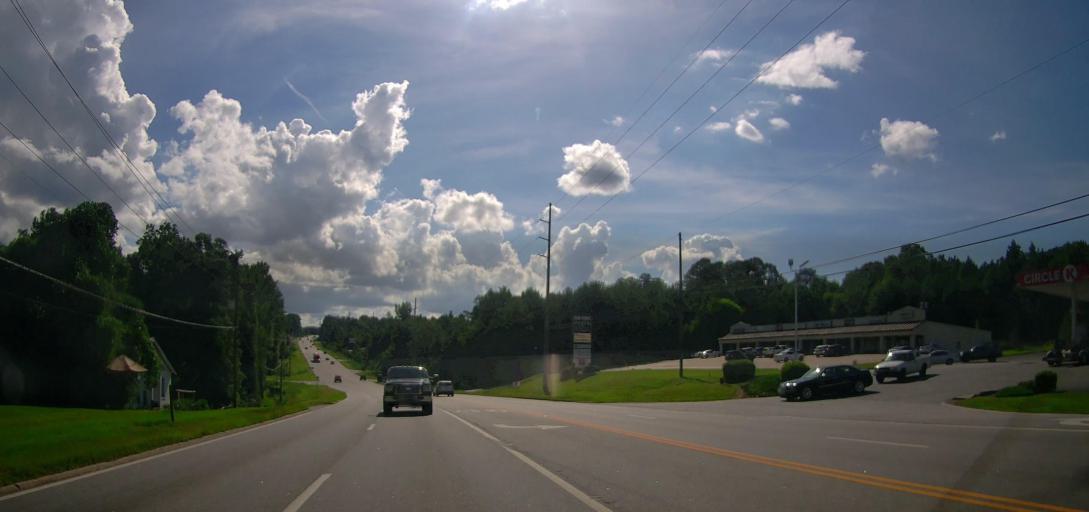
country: US
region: Alabama
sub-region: Russell County
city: Phenix City
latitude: 32.4757
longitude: -85.0396
